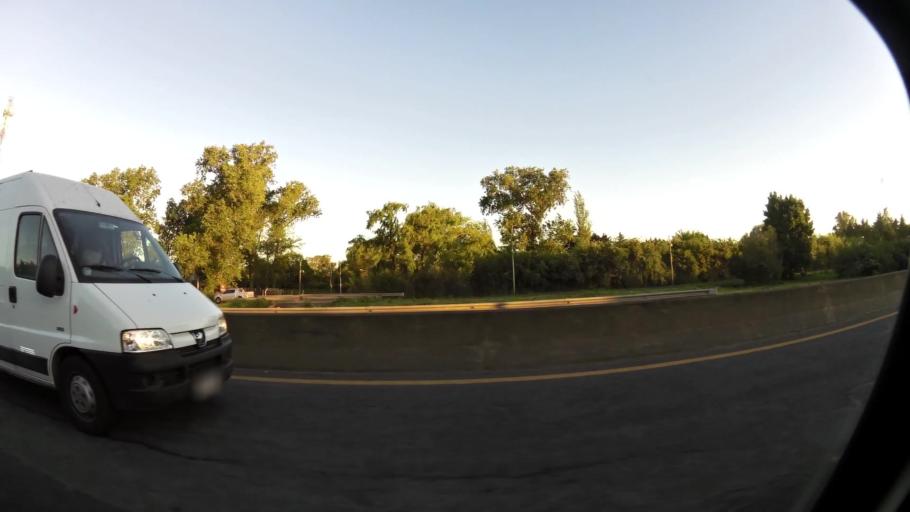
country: AR
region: Buenos Aires
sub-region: Partido de Quilmes
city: Quilmes
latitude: -34.8106
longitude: -58.1760
